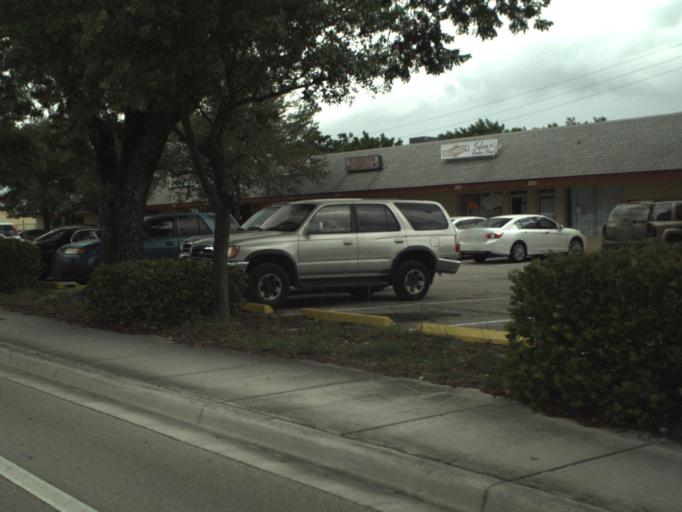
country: US
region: Florida
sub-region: Broward County
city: Pompano Beach Highlands
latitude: 26.2965
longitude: -80.1078
